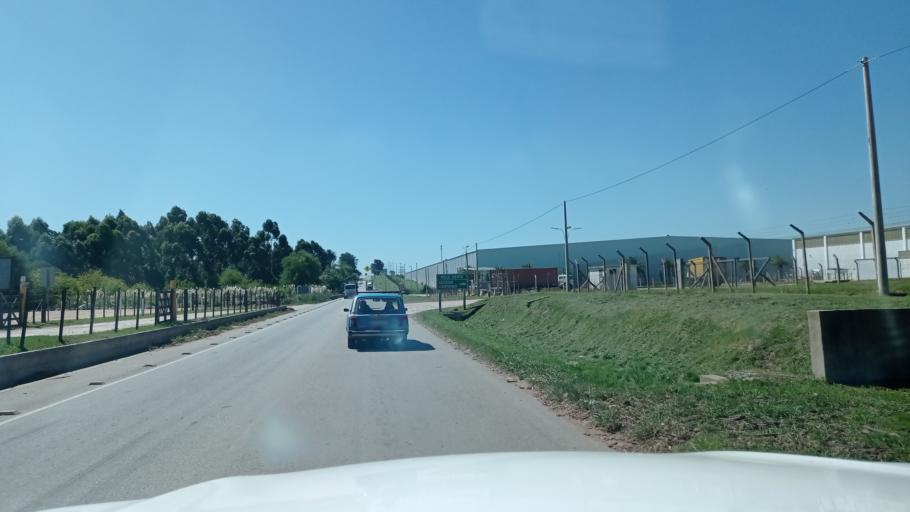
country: UY
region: Montevideo
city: Pajas Blancas
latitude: -34.8603
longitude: -56.2887
